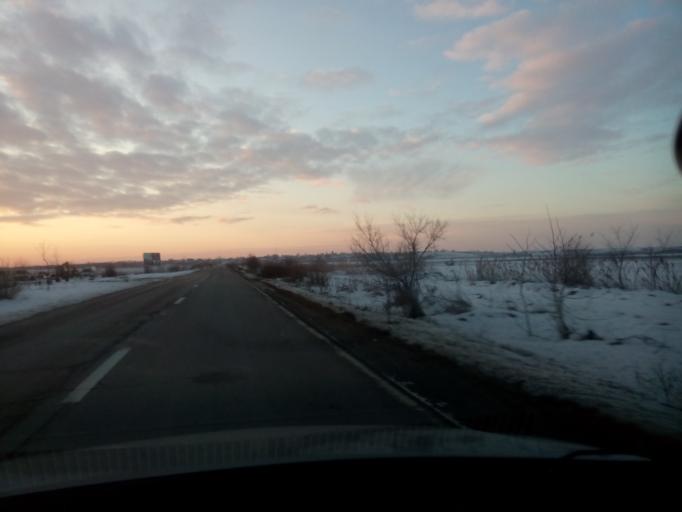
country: RO
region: Calarasi
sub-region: Comuna Budesti
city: Budesti
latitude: 44.2302
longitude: 26.4340
